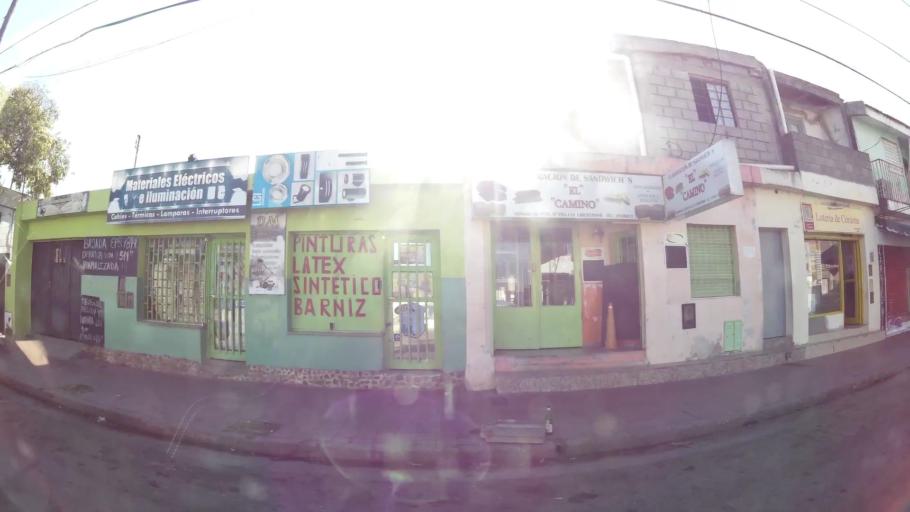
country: AR
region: Cordoba
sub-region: Departamento de Capital
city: Cordoba
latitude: -31.4719
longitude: -64.2246
